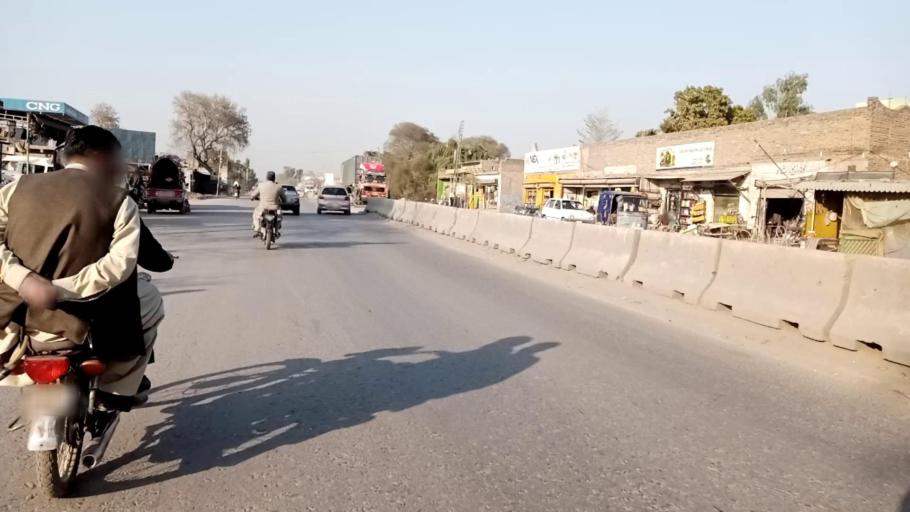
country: PK
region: Khyber Pakhtunkhwa
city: Peshawar
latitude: 33.9400
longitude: 71.5555
